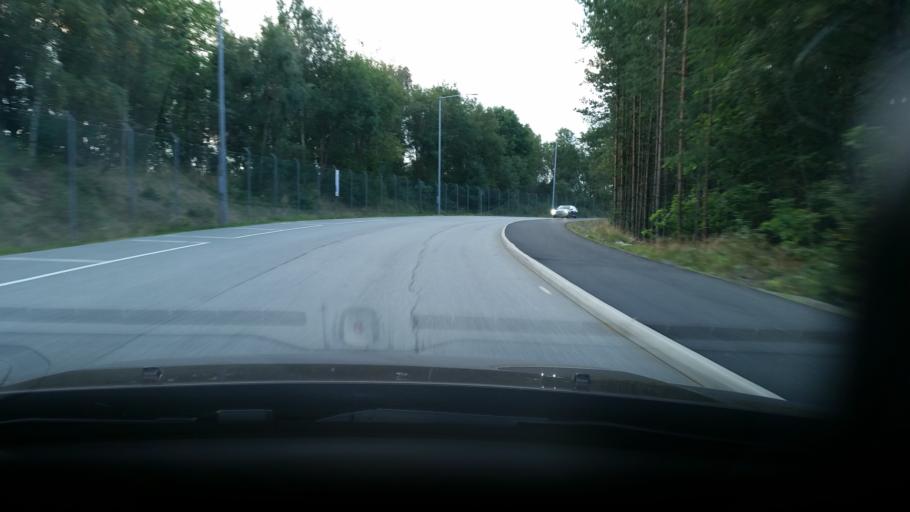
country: SE
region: Vaestra Goetaland
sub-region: Goteborg
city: Majorna
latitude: 57.7342
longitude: 11.8560
